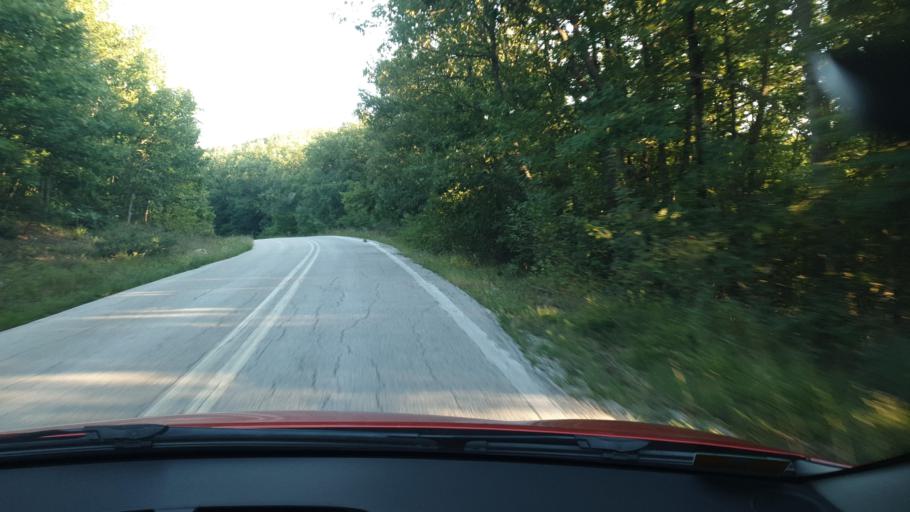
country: GR
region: Central Macedonia
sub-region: Nomos Chalkidikis
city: Galatista
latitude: 40.5344
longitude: 23.2771
